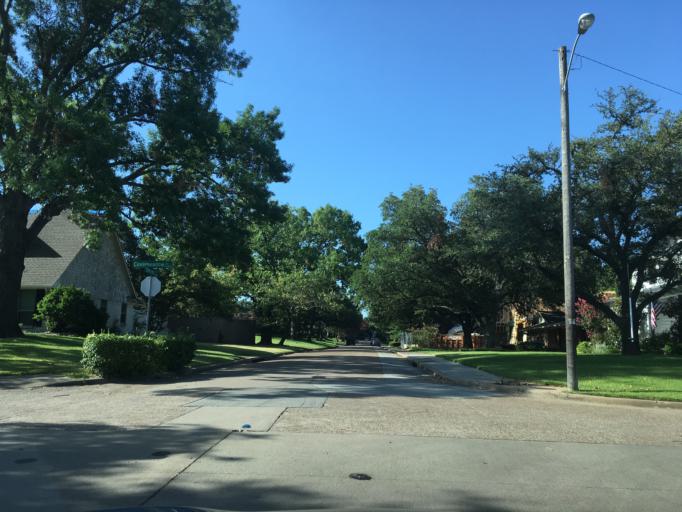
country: US
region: Texas
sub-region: Dallas County
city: Richardson
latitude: 32.8820
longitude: -96.7291
